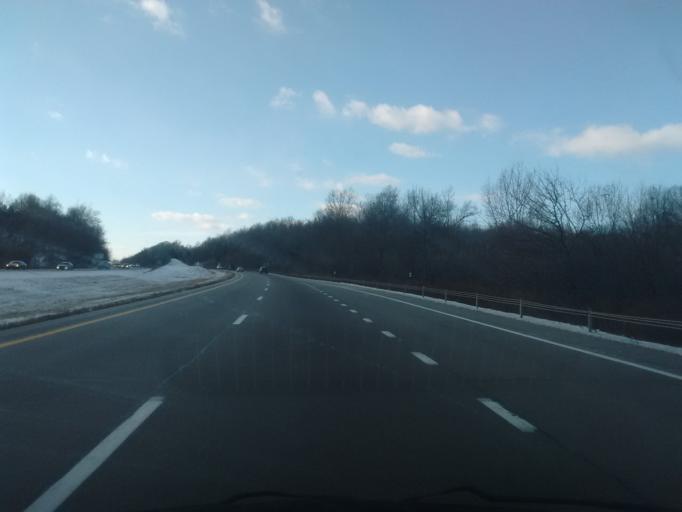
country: US
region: New York
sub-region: Dutchess County
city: Fishkill
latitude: 41.5295
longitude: -73.9212
